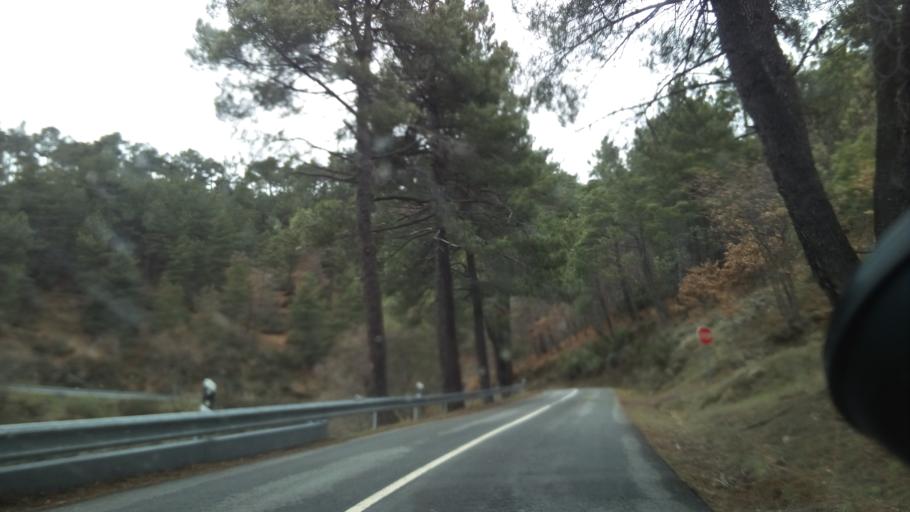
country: PT
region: Guarda
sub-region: Manteigas
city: Manteigas
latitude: 40.4136
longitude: -7.5308
